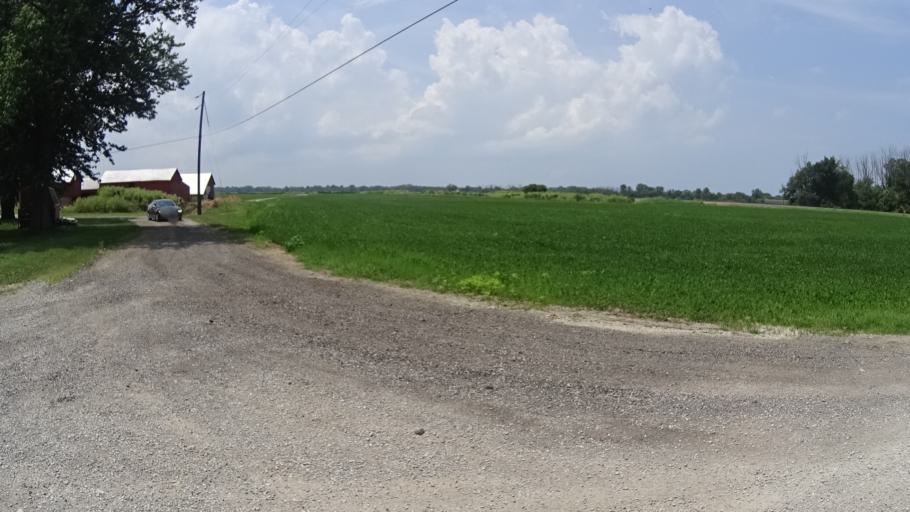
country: US
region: Ohio
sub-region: Lorain County
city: Vermilion
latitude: 41.4084
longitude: -82.3766
